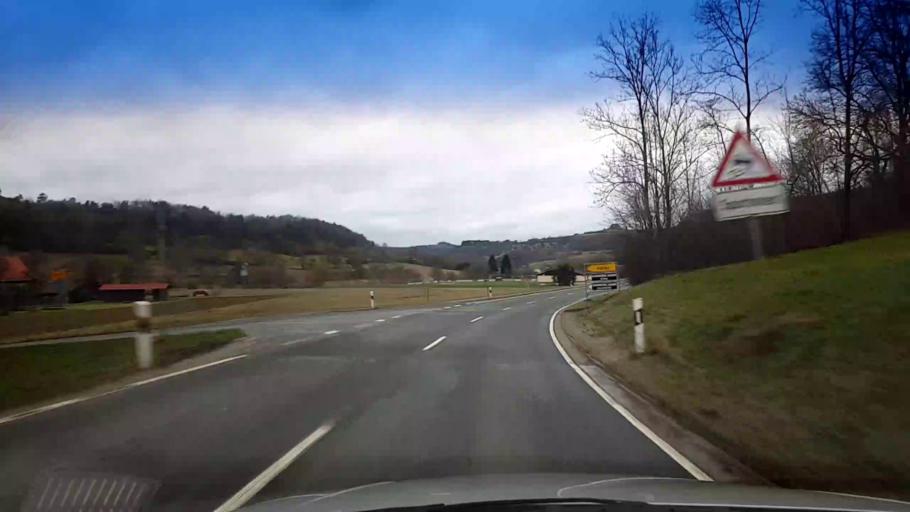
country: DE
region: Bavaria
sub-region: Upper Franconia
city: Wattendorf
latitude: 50.0569
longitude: 11.0751
